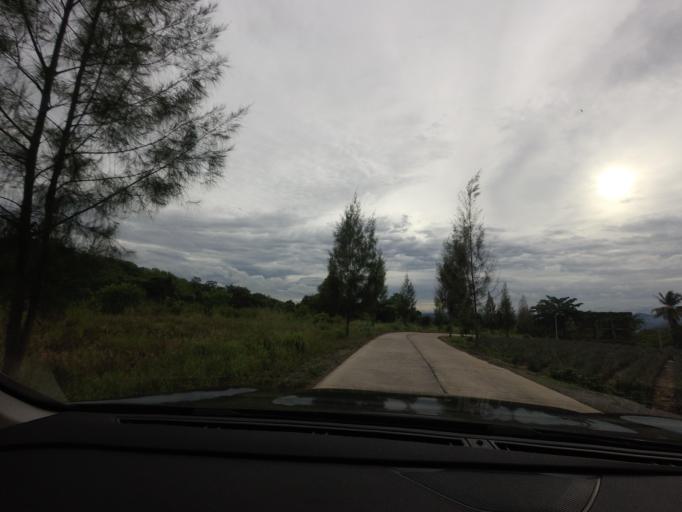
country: TH
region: Prachuap Khiri Khan
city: Hua Hin
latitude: 12.4818
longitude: 99.9402
